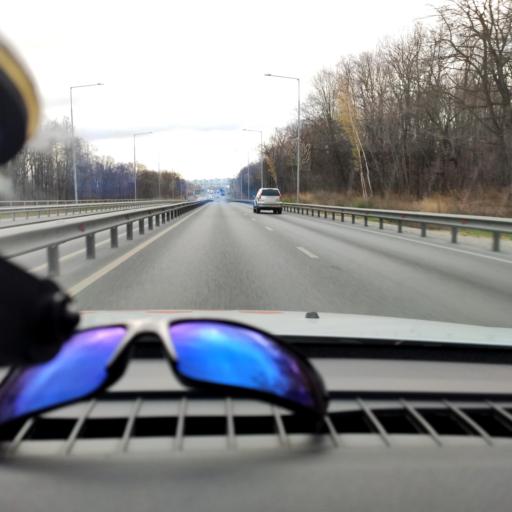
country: RU
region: Samara
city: Volzhskiy
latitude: 53.3600
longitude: 50.2064
